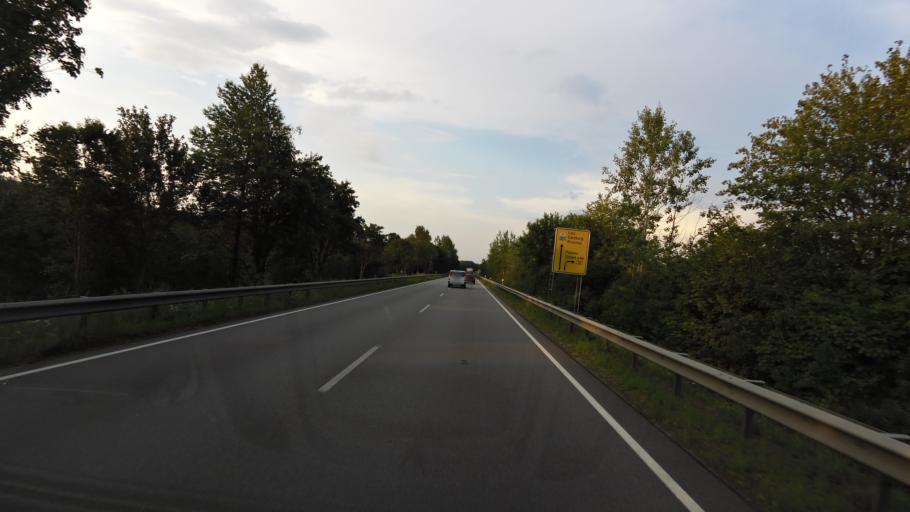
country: DE
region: Bavaria
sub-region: Lower Bavaria
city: Kirchdorf am Inn
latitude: 48.2454
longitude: 12.9934
